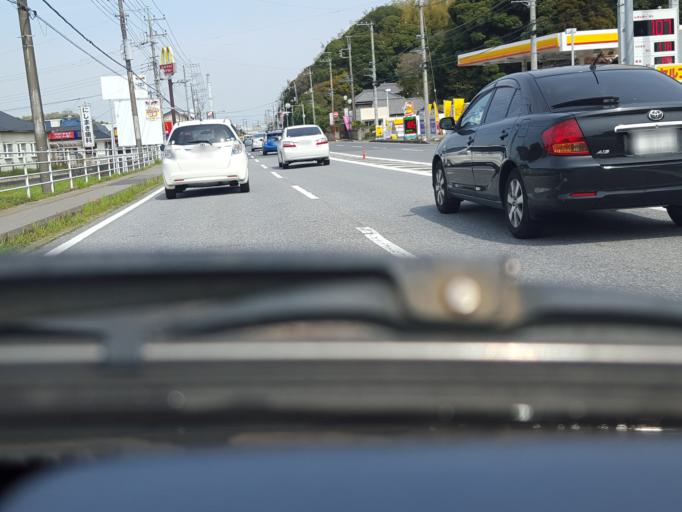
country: JP
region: Chiba
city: Ichihara
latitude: 35.4644
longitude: 140.0459
